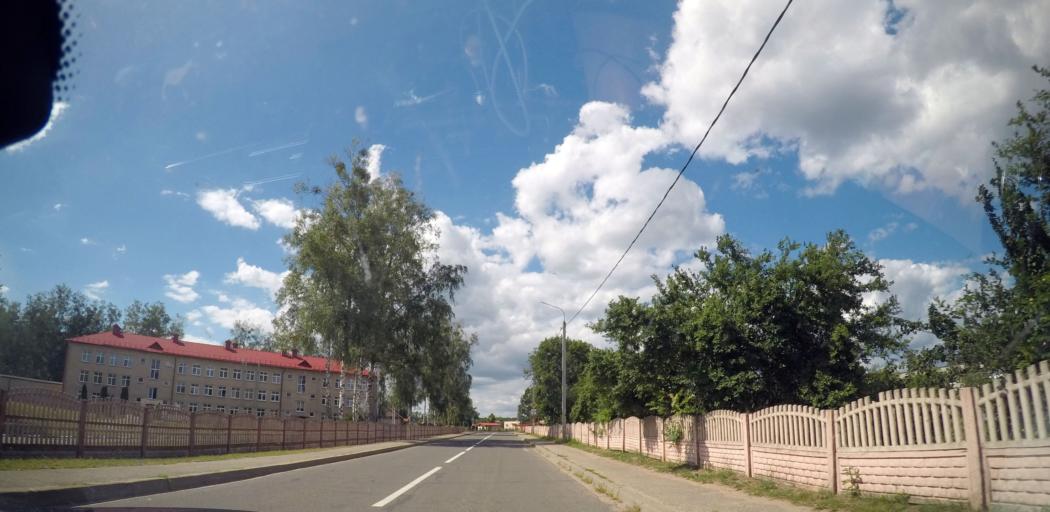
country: LT
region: Alytaus apskritis
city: Druskininkai
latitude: 53.8802
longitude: 24.1407
